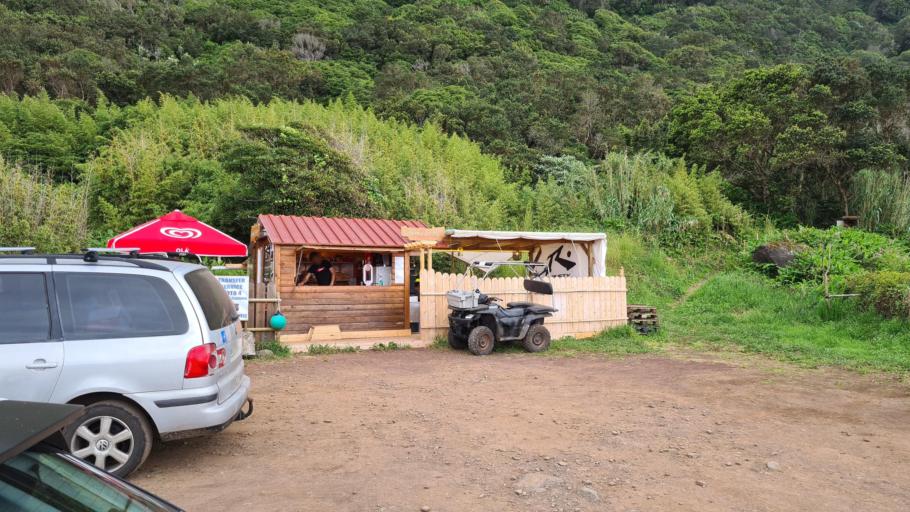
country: PT
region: Azores
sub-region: Sao Roque do Pico
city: Sao Roque do Pico
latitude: 38.6403
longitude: -27.9679
